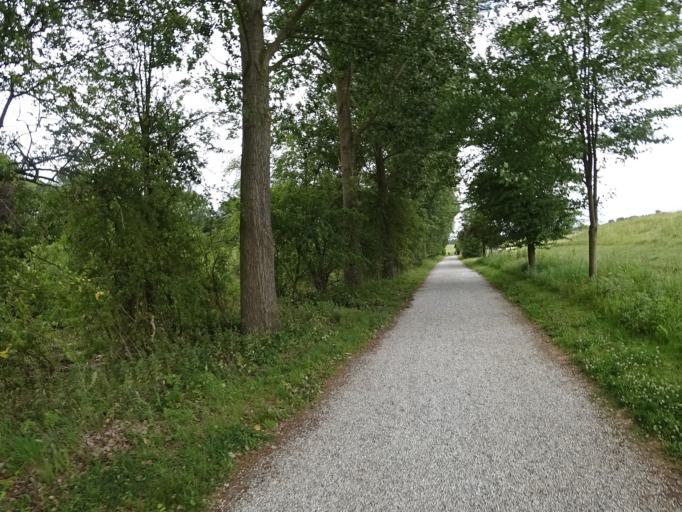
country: BE
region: Wallonia
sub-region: Province du Hainaut
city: Enghien
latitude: 50.6869
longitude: 4.0379
